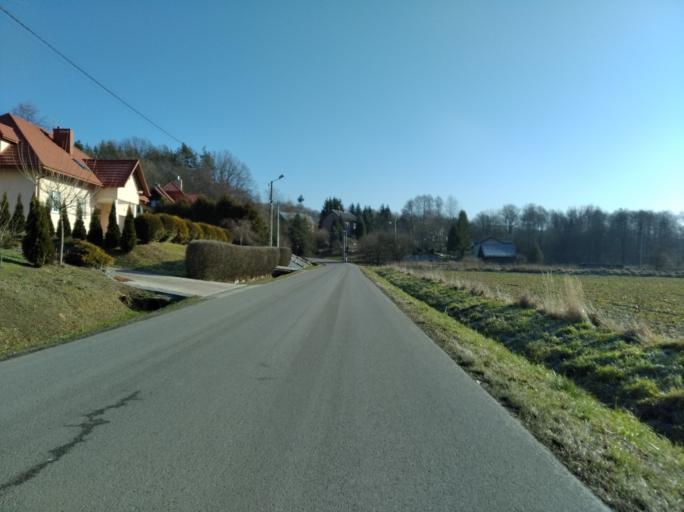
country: PL
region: Subcarpathian Voivodeship
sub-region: Powiat strzyzowski
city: Niebylec
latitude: 49.8555
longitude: 21.9121
